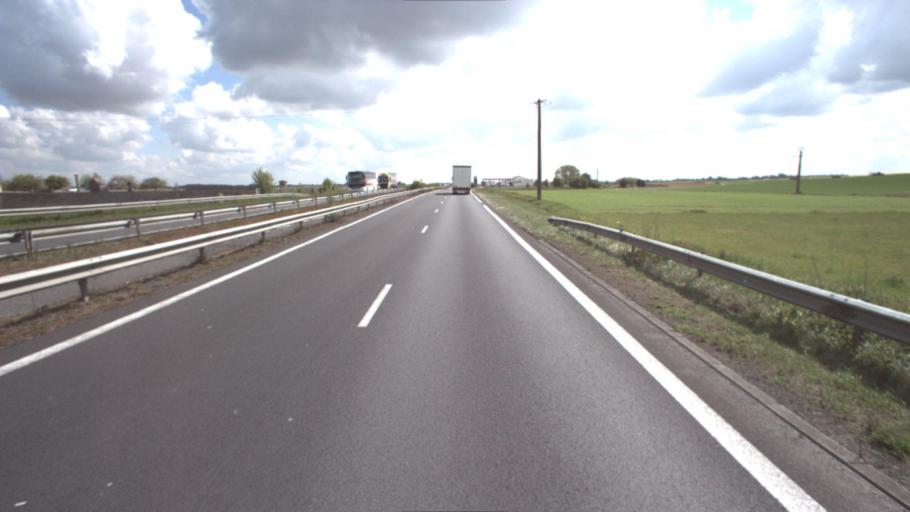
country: FR
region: Ile-de-France
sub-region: Departement de Seine-et-Marne
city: Jouy-le-Chatel
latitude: 48.6844
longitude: 3.0829
